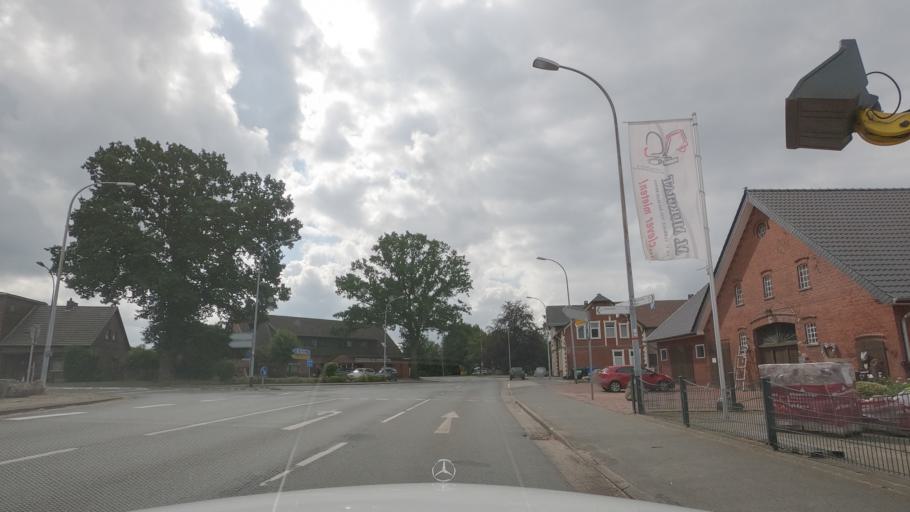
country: DE
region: Lower Saxony
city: Uthlede
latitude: 53.3085
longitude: 8.5798
